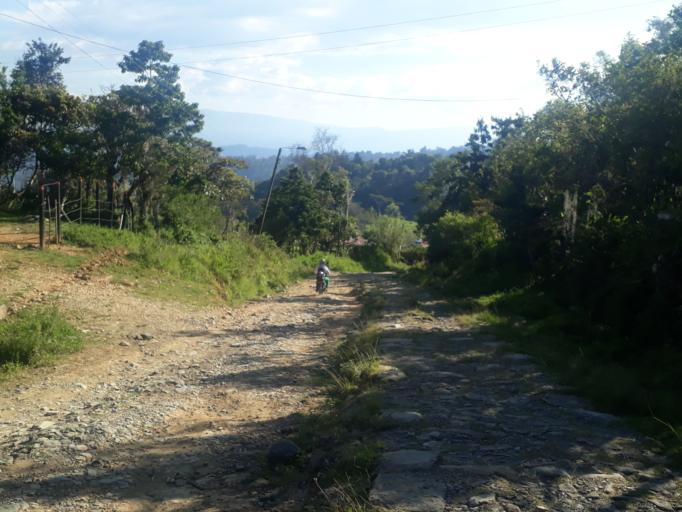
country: CO
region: Santander
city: Velez
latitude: 6.0262
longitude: -73.6671
